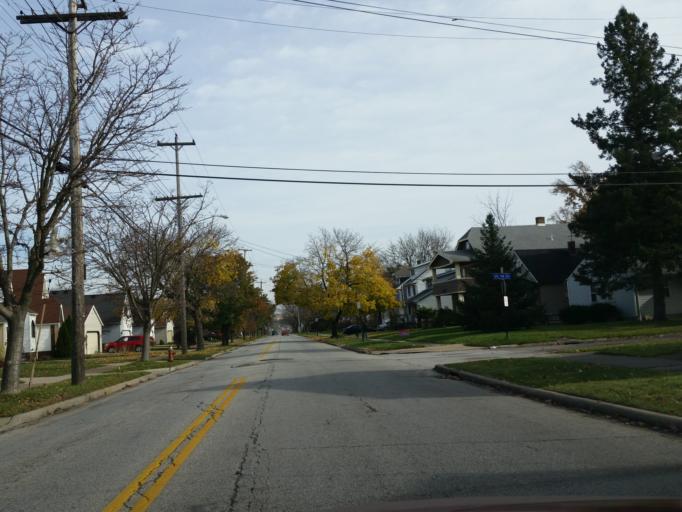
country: US
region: Ohio
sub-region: Cuyahoga County
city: Brooklyn Heights
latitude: 41.4350
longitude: -81.6902
